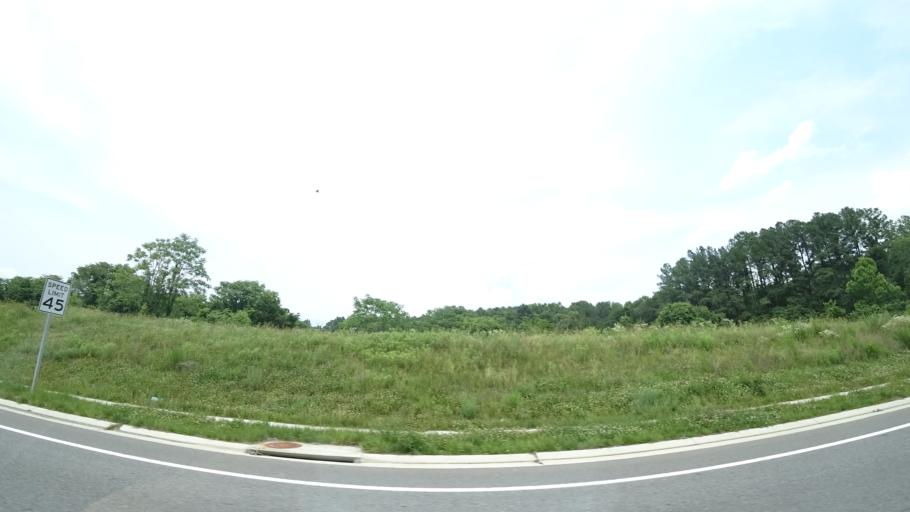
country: US
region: Virginia
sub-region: Fairfax County
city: Lorton
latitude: 38.7052
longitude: -77.2324
